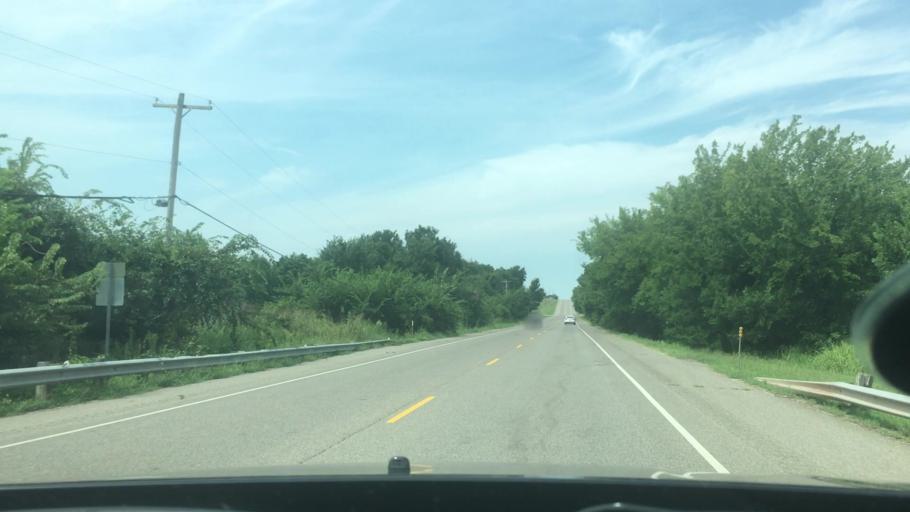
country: US
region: Oklahoma
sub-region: Pottawatomie County
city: Shawnee
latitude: 35.3331
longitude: -96.8121
